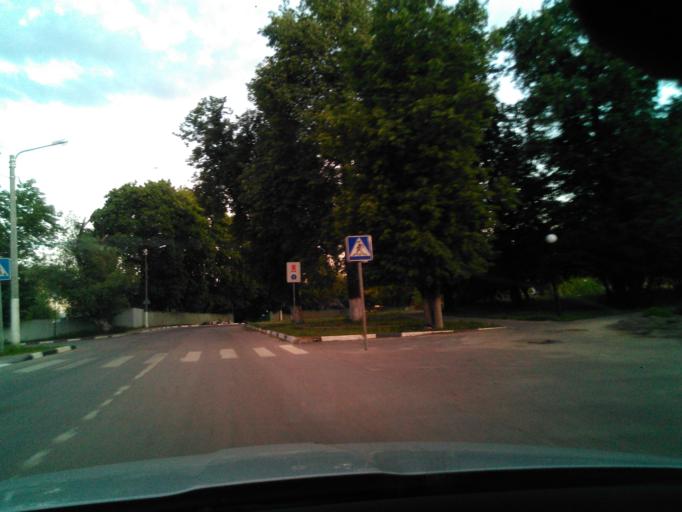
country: RU
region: Moskovskaya
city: Dolgoprudnyy
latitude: 55.9525
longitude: 37.5071
